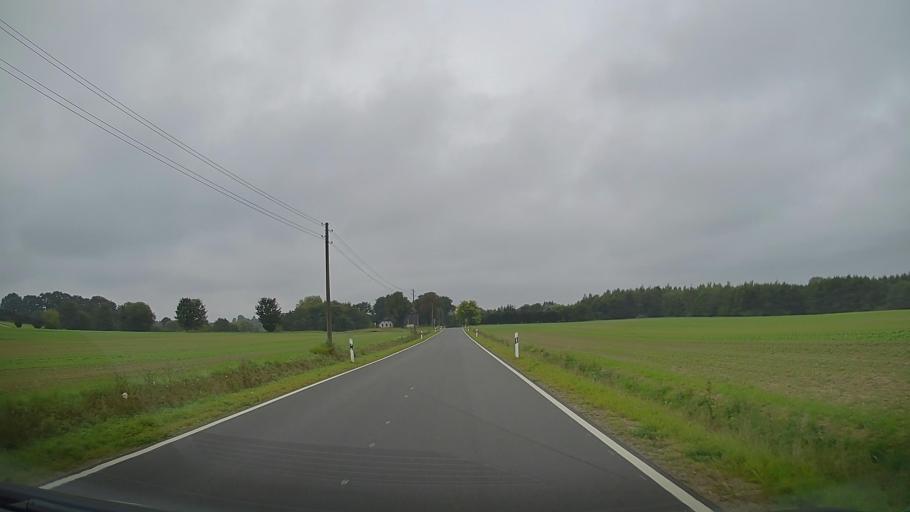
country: DE
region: Mecklenburg-Vorpommern
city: Kavelstorf
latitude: 53.9268
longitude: 12.2026
